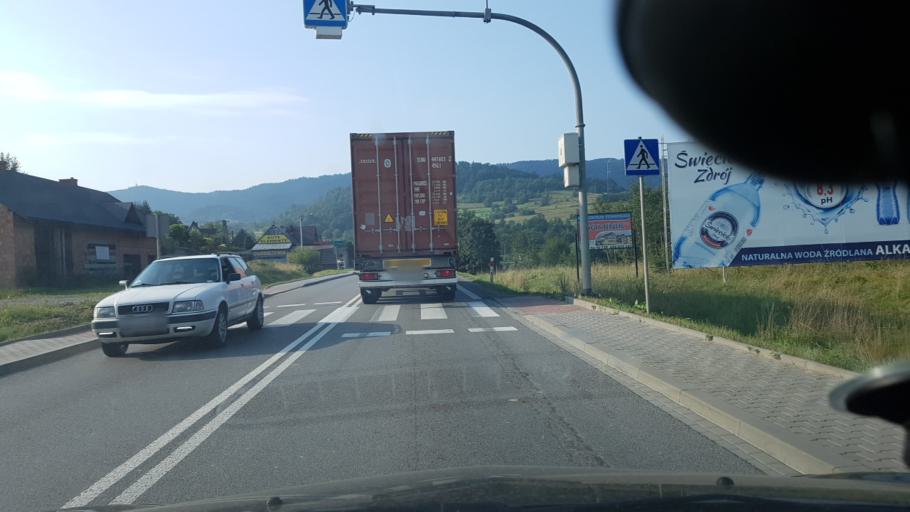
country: PL
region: Lesser Poland Voivodeship
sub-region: Powiat myslenicki
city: Lubien
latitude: 49.6927
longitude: 19.9573
